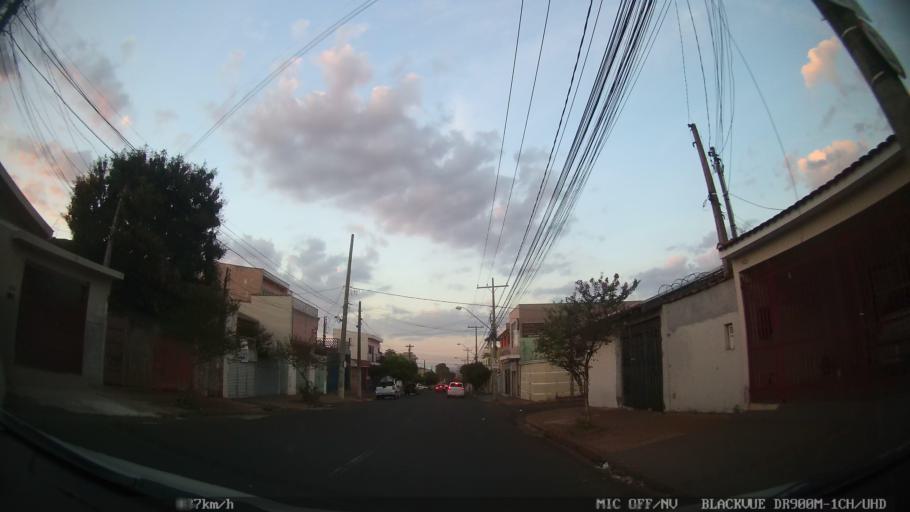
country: BR
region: Sao Paulo
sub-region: Ribeirao Preto
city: Ribeirao Preto
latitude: -21.1536
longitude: -47.8263
